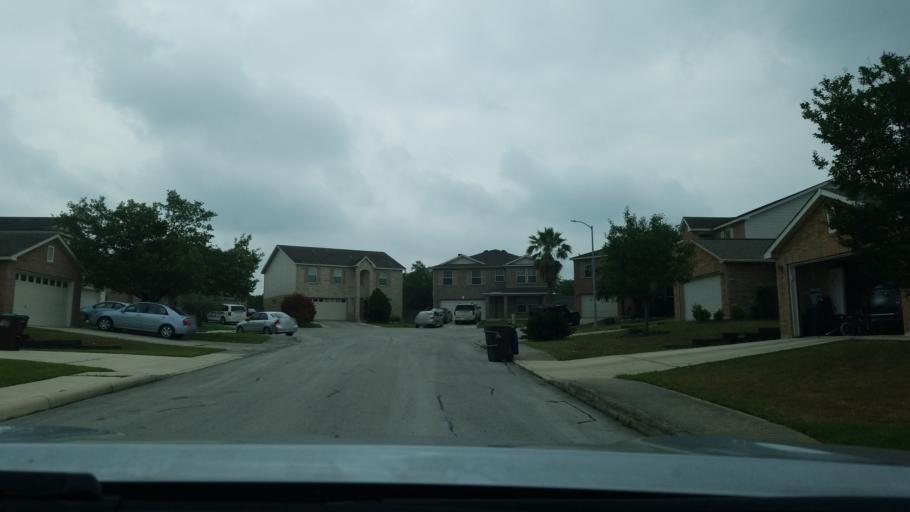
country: US
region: Texas
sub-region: Bexar County
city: Timberwood Park
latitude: 29.6853
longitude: -98.4621
